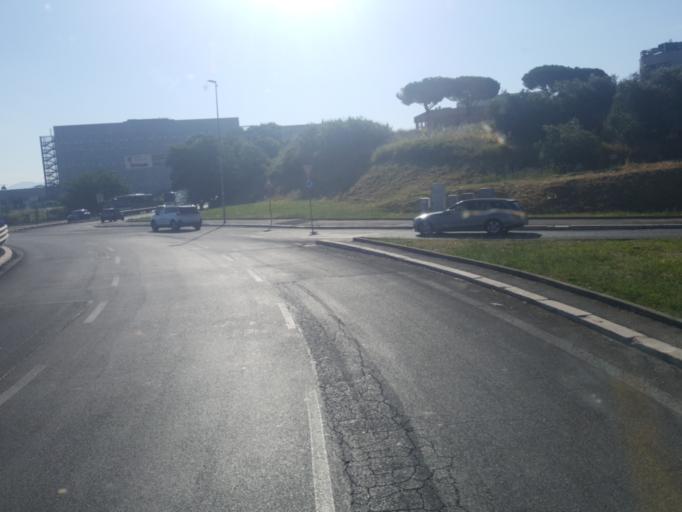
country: IT
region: Latium
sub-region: Citta metropolitana di Roma Capitale
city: Frascati
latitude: 41.8562
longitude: 12.6254
